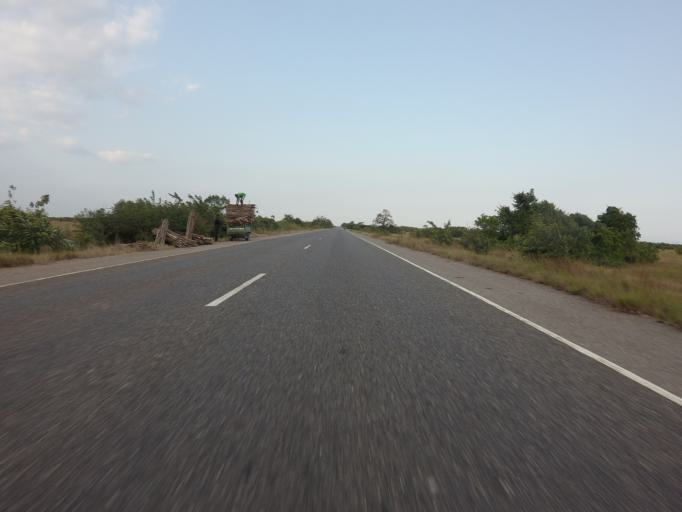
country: GH
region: Volta
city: Anloga
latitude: 6.0823
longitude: 0.5688
